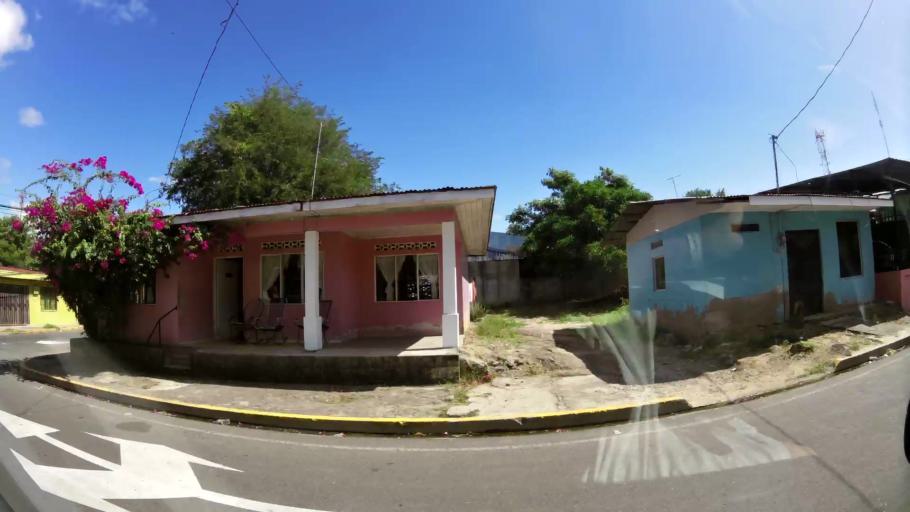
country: CR
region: Guanacaste
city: Bagaces
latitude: 10.5288
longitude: -85.2555
